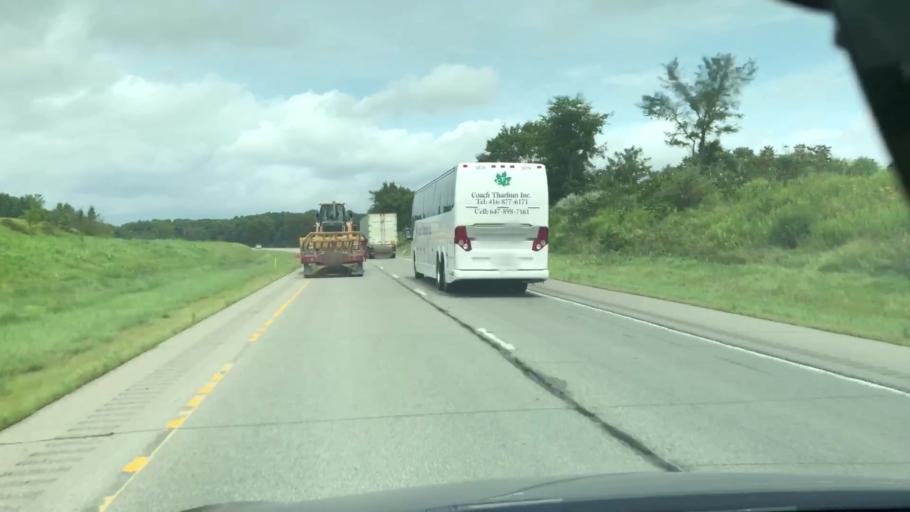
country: US
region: Pennsylvania
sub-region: Butler County
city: Slippery Rock
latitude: 41.0627
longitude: -80.1231
